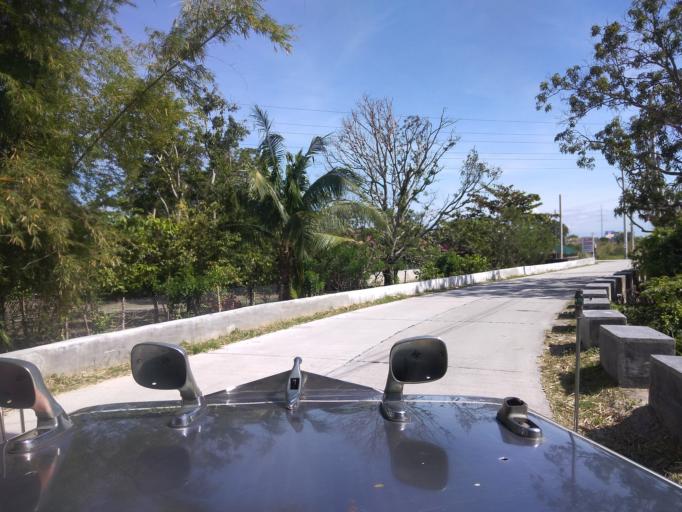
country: PH
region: Central Luzon
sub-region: Province of Pampanga
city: Magliman
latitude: 15.0259
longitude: 120.6665
